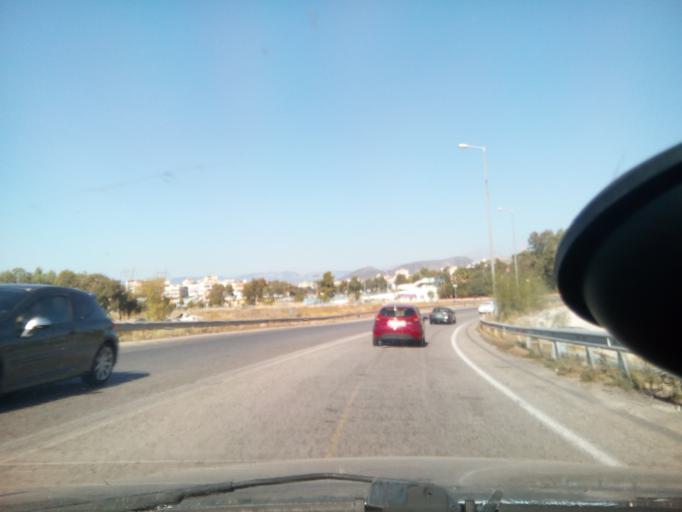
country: GR
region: Central Greece
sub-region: Nomos Evvoias
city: Chalkida
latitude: 38.4547
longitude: 23.6062
